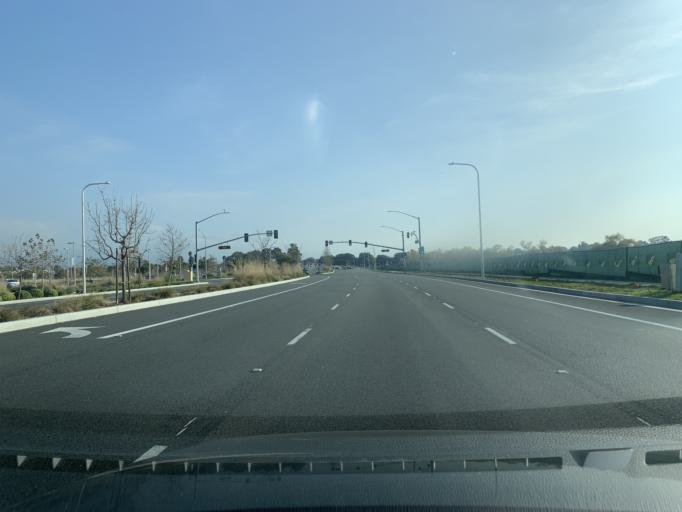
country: US
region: California
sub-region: Orange County
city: Laguna Woods
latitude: 33.6474
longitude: -117.7292
